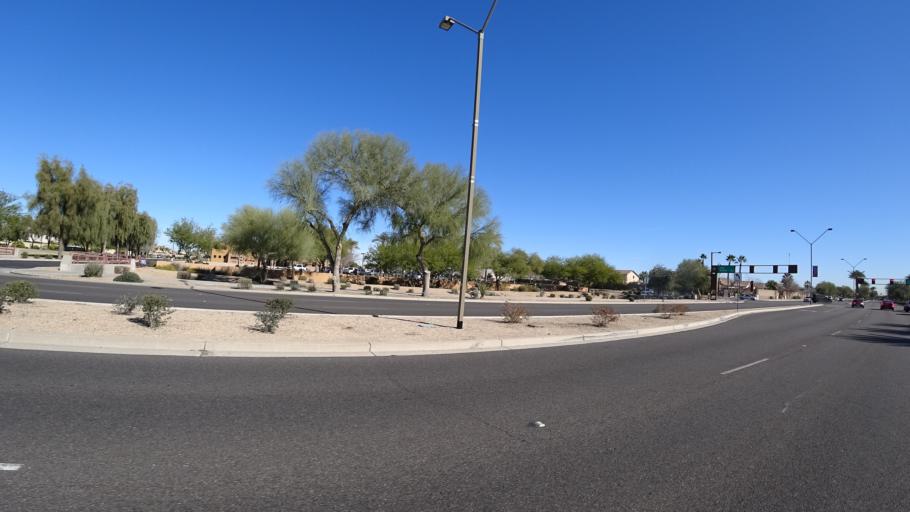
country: US
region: Arizona
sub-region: Maricopa County
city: Litchfield Park
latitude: 33.4858
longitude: -112.3698
